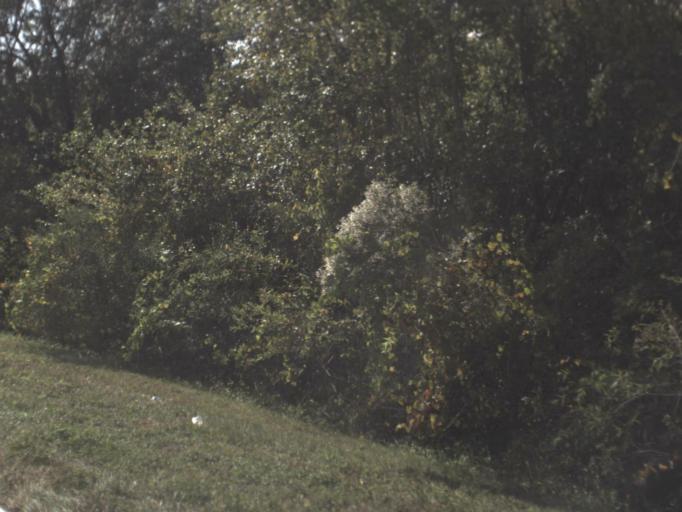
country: US
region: Florida
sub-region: Osceola County
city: Campbell
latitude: 28.2164
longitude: -81.4793
